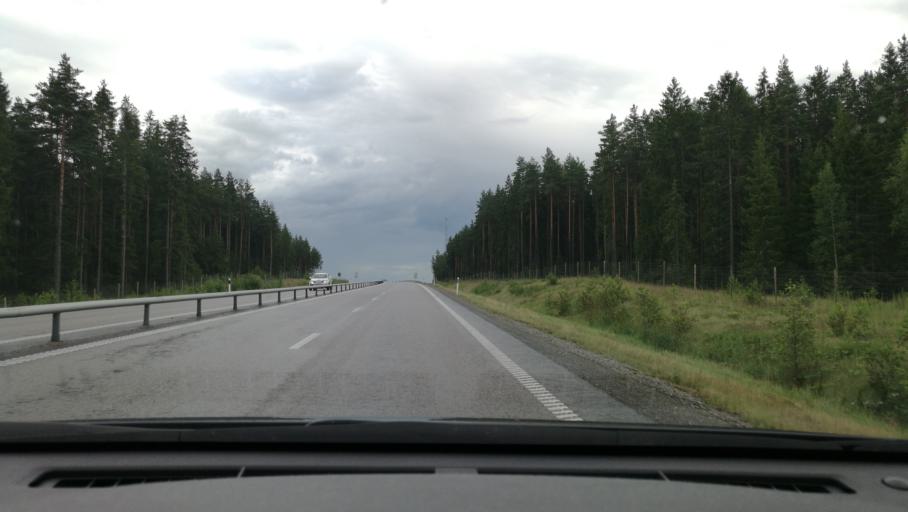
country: SE
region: Soedermanland
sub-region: Katrineholms Kommun
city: Katrineholm
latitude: 59.0043
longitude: 16.2452
